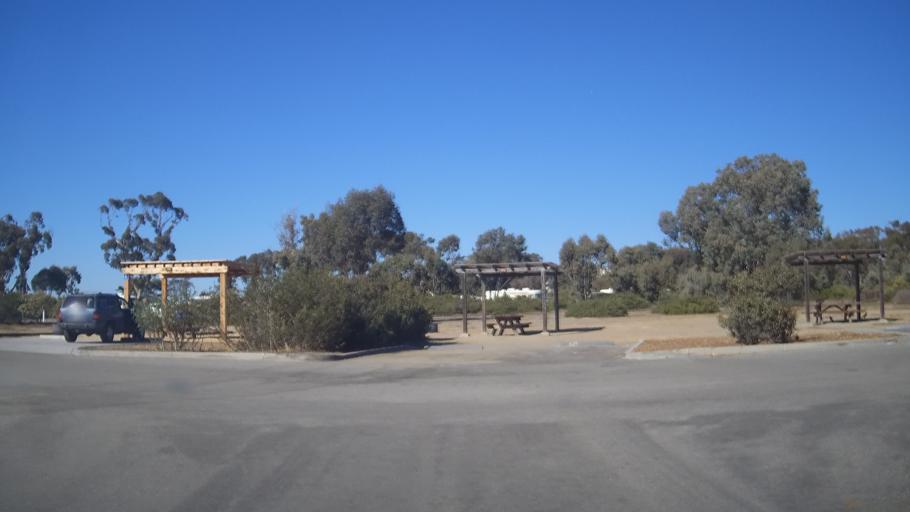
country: US
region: California
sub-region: Orange County
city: San Clemente
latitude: 33.4034
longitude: -117.6003
